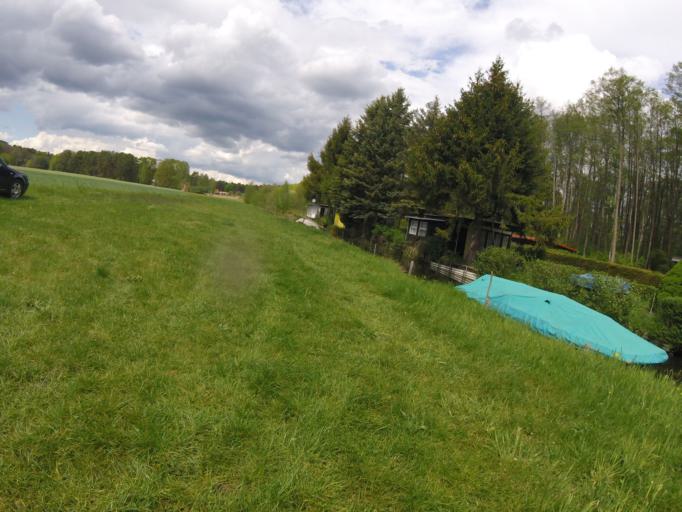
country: DE
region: Brandenburg
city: Gross Koris
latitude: 52.1668
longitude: 13.6521
